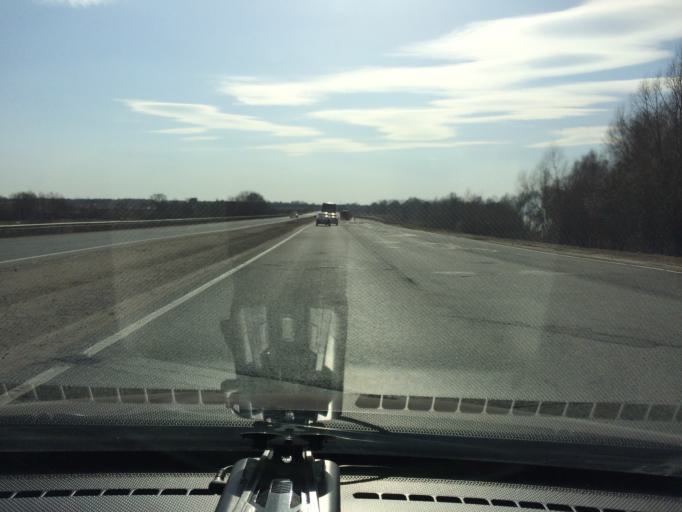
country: RU
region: Mariy-El
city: Yoshkar-Ola
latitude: 56.6889
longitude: 48.0467
